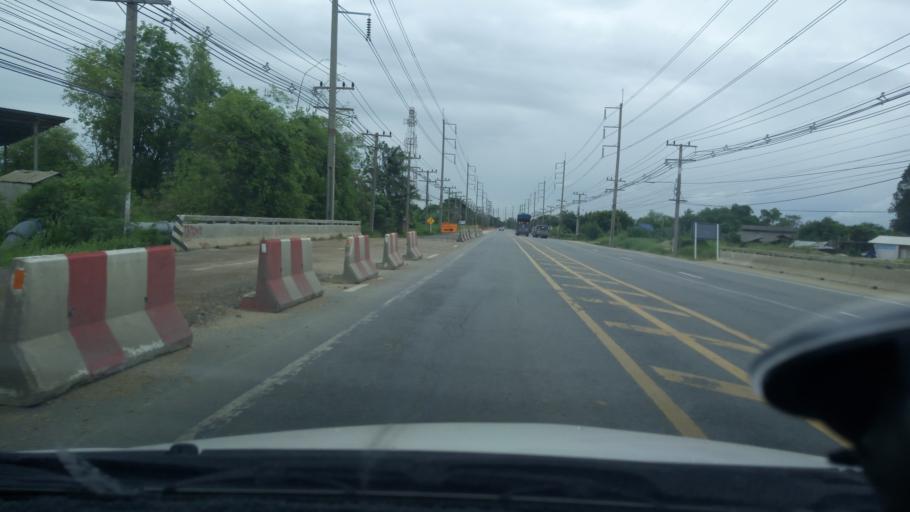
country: TH
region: Chon Buri
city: Phanat Nikhom
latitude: 13.4892
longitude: 101.1661
